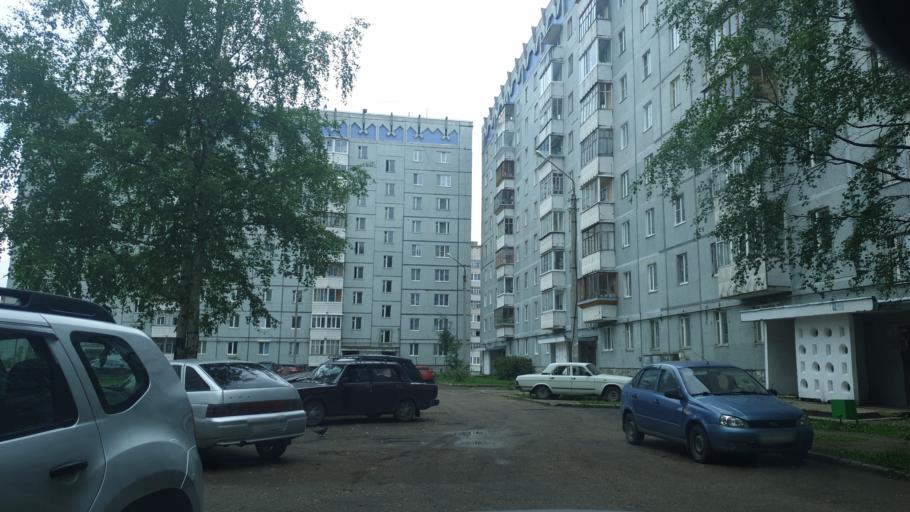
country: RU
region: Komi Republic
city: Ezhva
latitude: 61.7829
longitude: 50.7548
